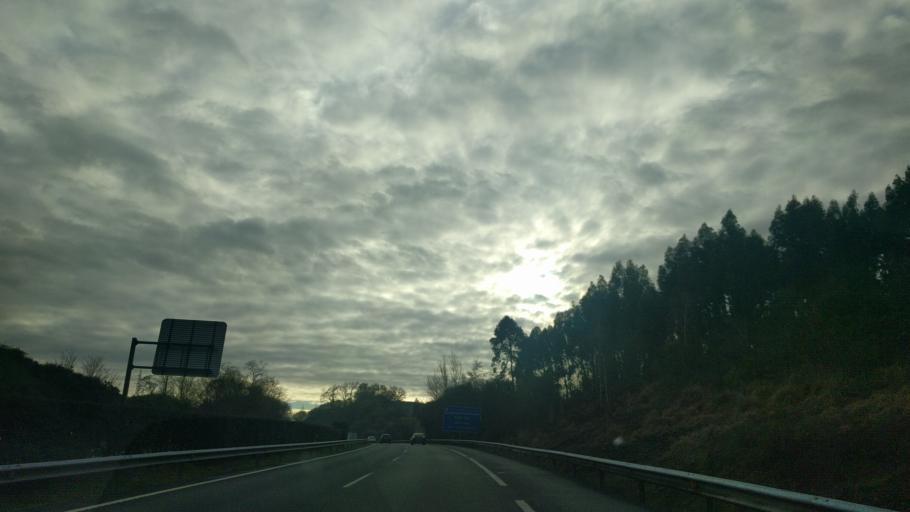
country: ES
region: Cantabria
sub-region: Provincia de Cantabria
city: Colindres
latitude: 43.3927
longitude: -3.4803
